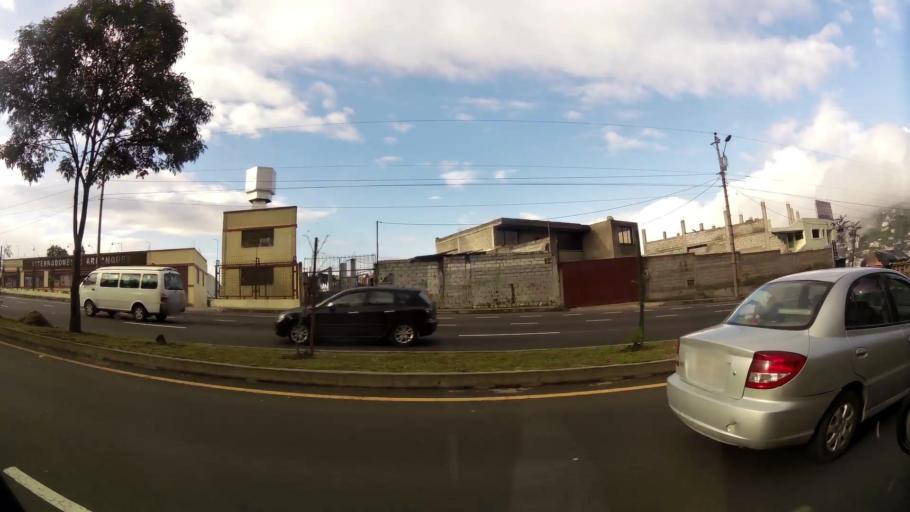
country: EC
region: Pichincha
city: Quito
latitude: -0.2322
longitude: -78.4897
